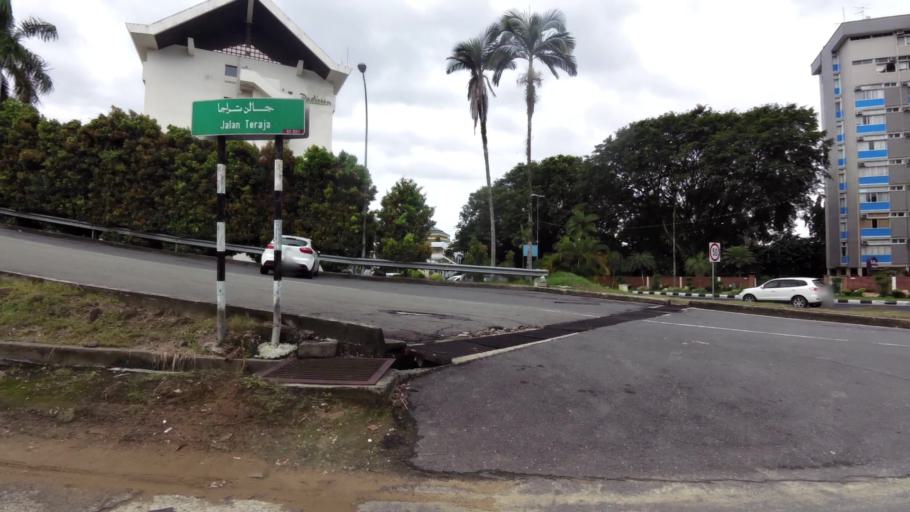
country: BN
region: Brunei and Muara
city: Bandar Seri Begawan
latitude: 4.8950
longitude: 114.9420
